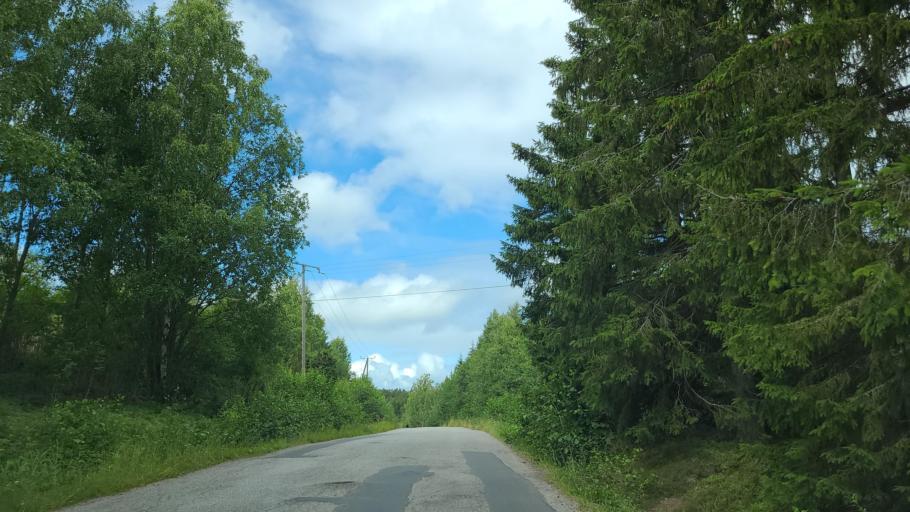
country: FI
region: Varsinais-Suomi
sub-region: Aboland-Turunmaa
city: Nagu
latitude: 60.1706
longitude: 21.9811
